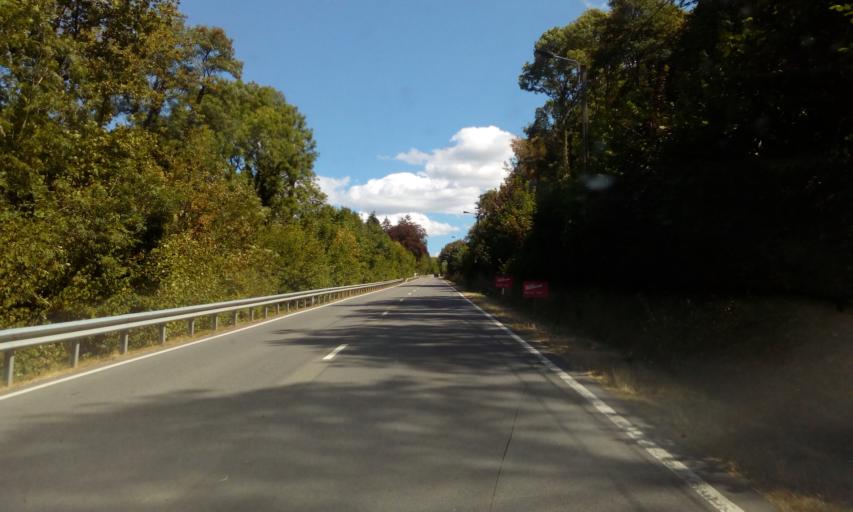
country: BE
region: Wallonia
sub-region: Province de Namur
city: Beauraing
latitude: 50.1075
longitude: 4.9641
